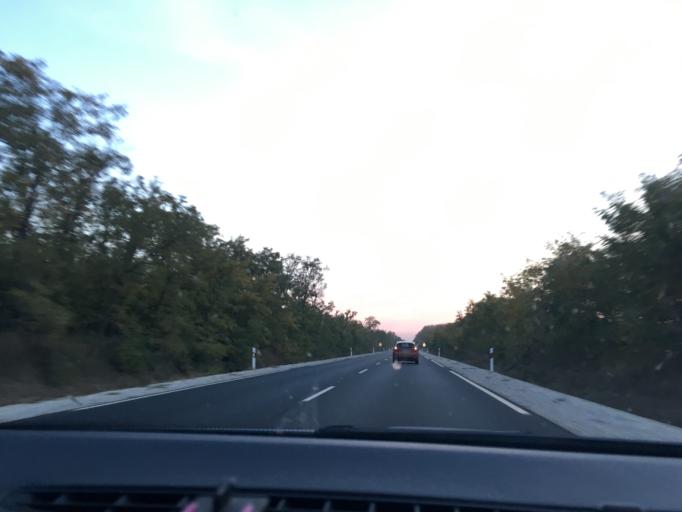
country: HU
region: Hajdu-Bihar
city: Hajduhadhaz
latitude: 47.6205
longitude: 21.6595
